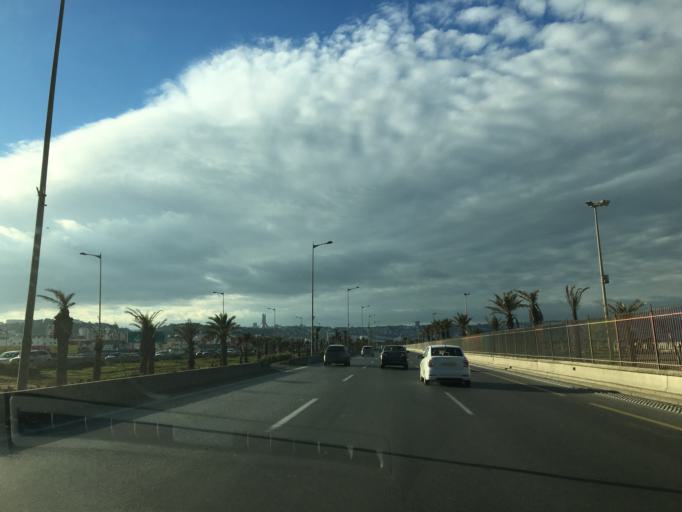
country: DZ
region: Alger
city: Birkhadem
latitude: 36.7436
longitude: 3.1103
